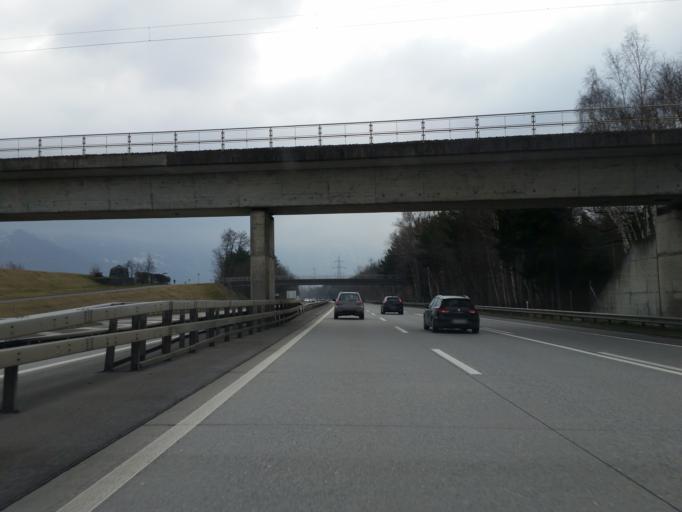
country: CH
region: Saint Gallen
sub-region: Wahlkreis Werdenberg
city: Buchs
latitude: 47.1646
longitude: 9.4886
